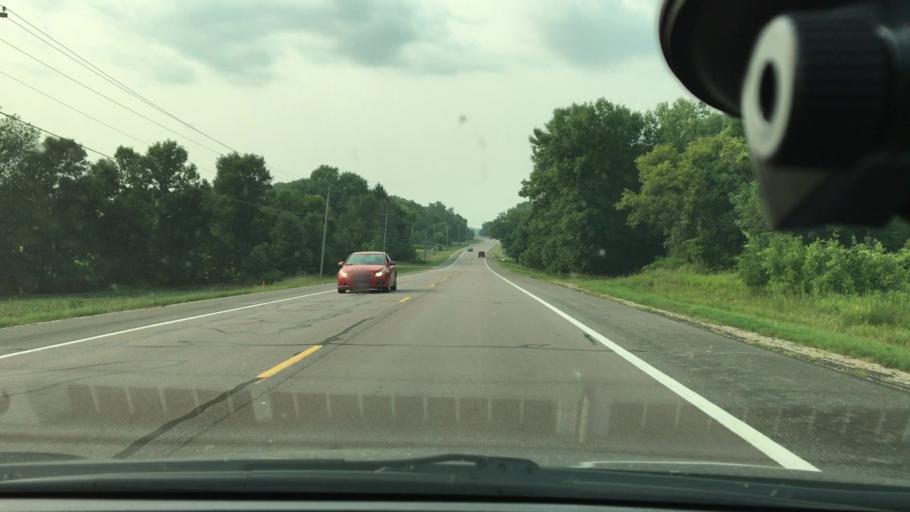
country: US
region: Minnesota
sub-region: Hennepin County
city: Dayton
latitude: 45.2488
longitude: -93.5343
